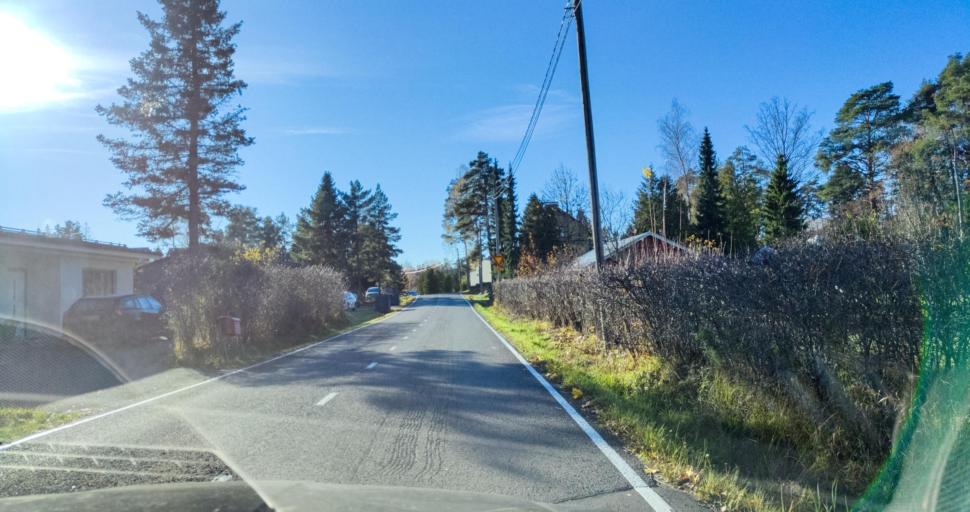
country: FI
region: Varsinais-Suomi
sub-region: Turku
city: Turku
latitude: 60.3963
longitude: 22.2054
